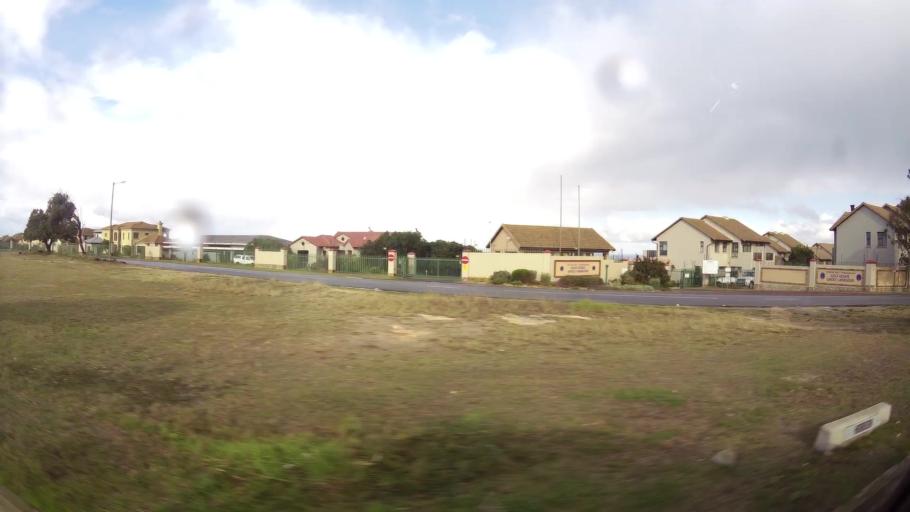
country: ZA
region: Western Cape
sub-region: Eden District Municipality
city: Mossel Bay
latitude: -34.1897
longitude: 22.1227
